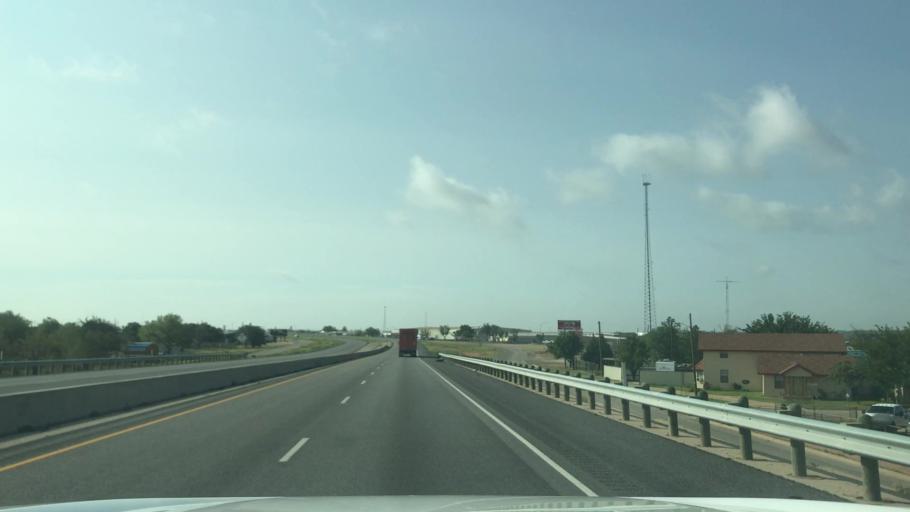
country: US
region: Texas
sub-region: Scurry County
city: Snyder
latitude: 32.7463
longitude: -100.9239
